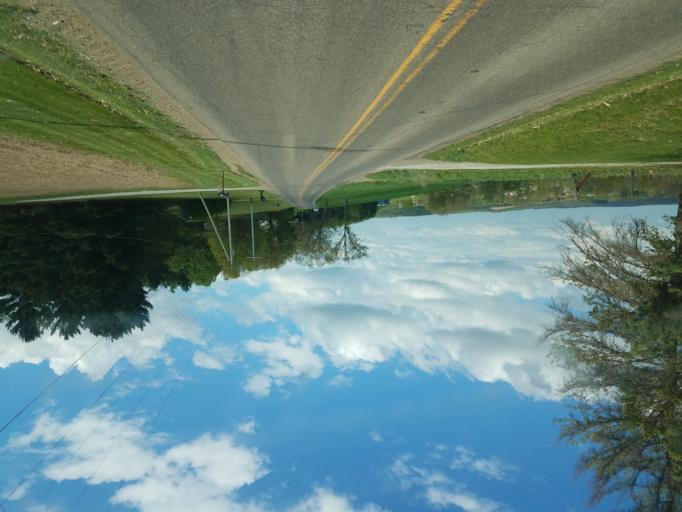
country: US
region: Ohio
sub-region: Knox County
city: Danville
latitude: 40.4533
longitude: -82.2766
